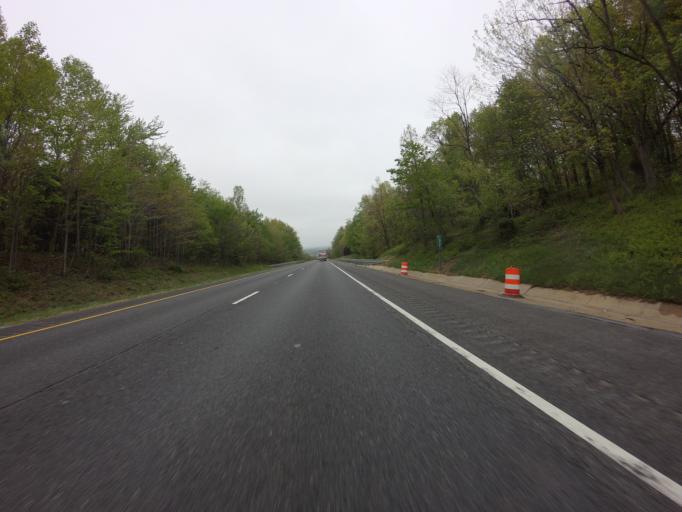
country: US
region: Maryland
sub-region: Washington County
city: Boonsboro
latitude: 39.5579
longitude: -77.6122
